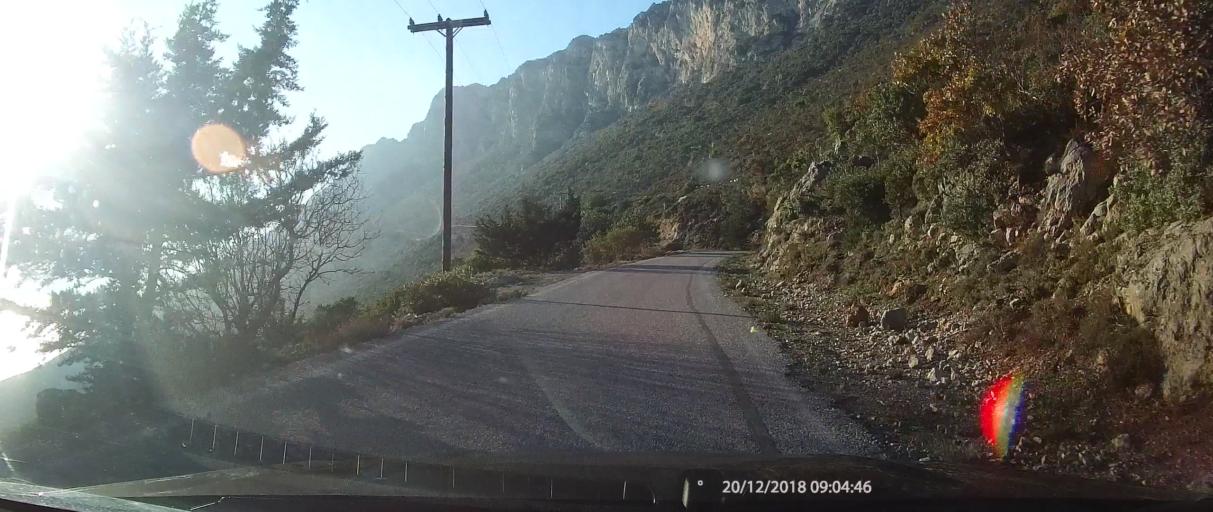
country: GR
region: Peloponnese
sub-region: Nomos Lakonias
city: Sykea
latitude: 36.9455
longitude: 22.9959
